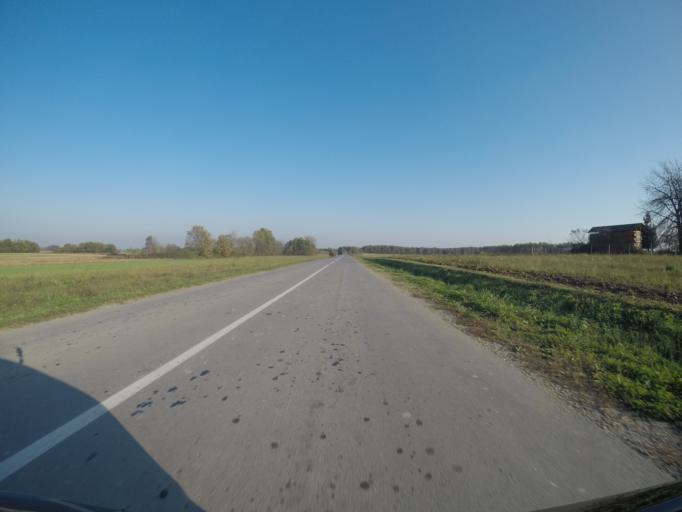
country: HR
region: Virovitick-Podravska
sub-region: Grad Virovitica
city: Virovitica
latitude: 45.8831
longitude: 17.3887
